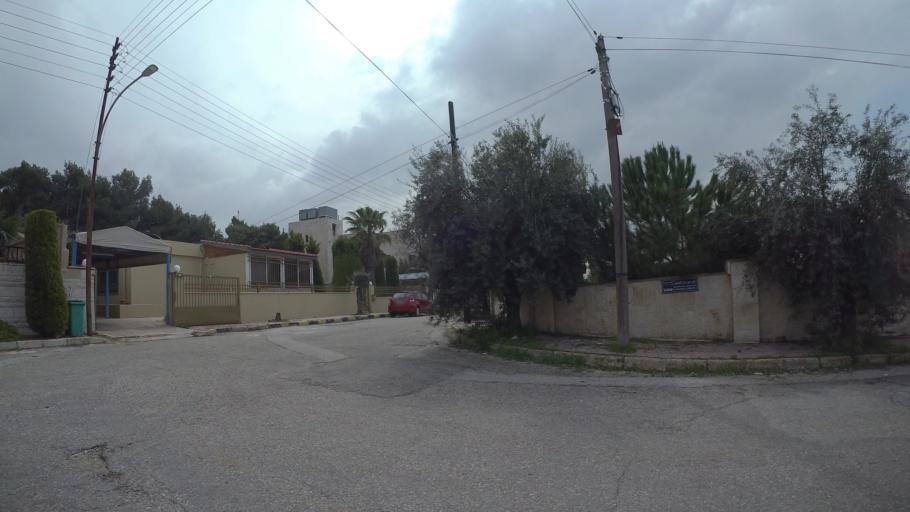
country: JO
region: Amman
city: Umm as Summaq
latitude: 31.8948
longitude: 35.8590
